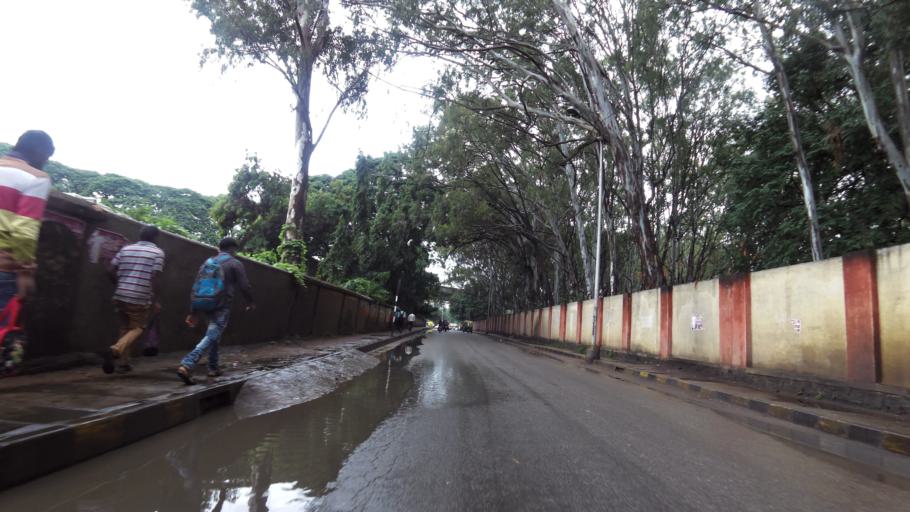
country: IN
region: Karnataka
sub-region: Bangalore Urban
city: Bangalore
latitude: 12.9862
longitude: 77.6427
